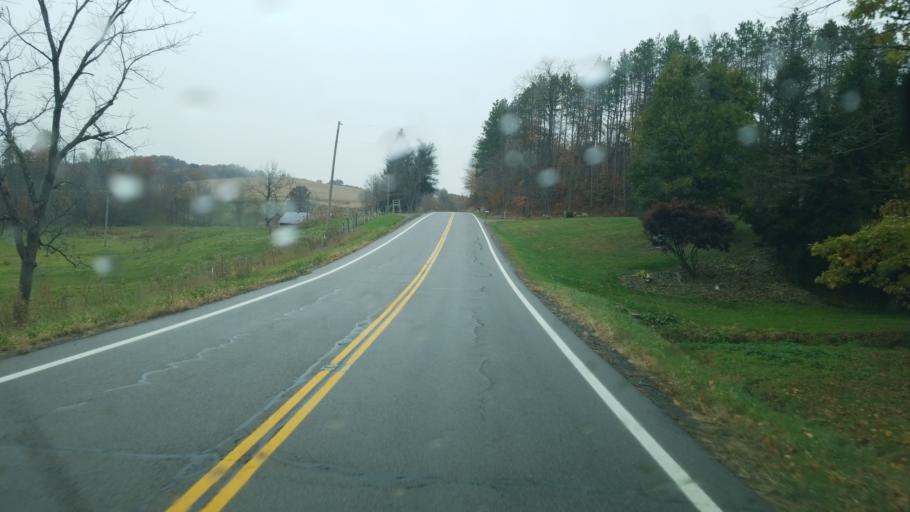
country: US
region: Ohio
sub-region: Coshocton County
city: Coshocton
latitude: 40.3905
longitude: -81.8708
